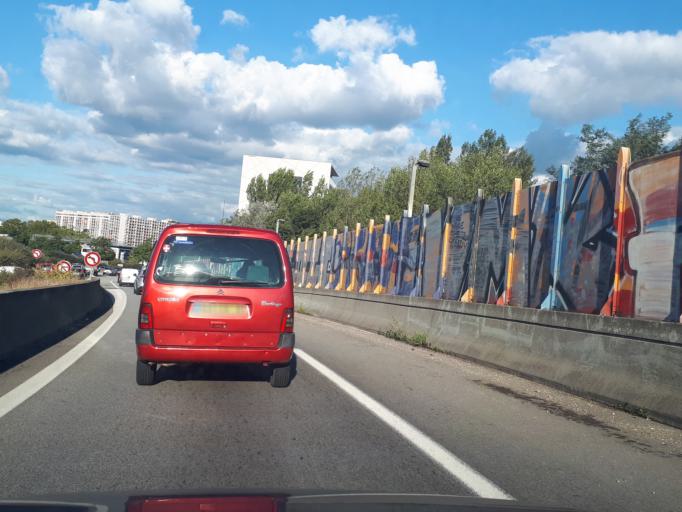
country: FR
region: Rhone-Alpes
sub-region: Departement de l'Isere
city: Grenoble
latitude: 45.1576
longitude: 5.7014
